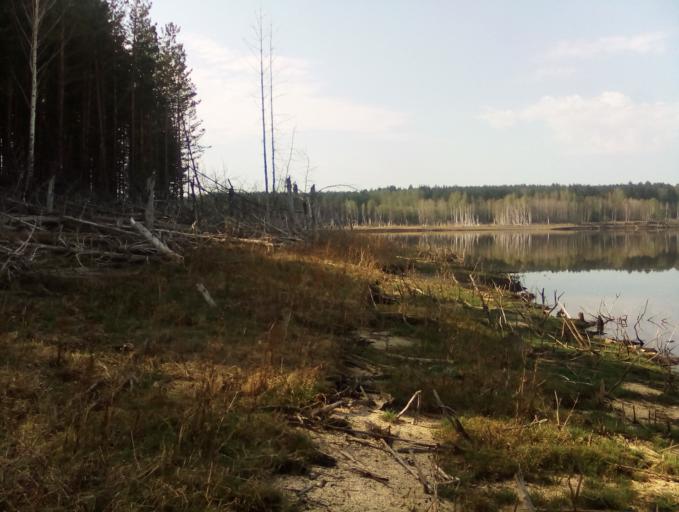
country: RU
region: Chelyabinsk
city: Nizhniy Ufaley
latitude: 55.7548
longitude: 60.1268
